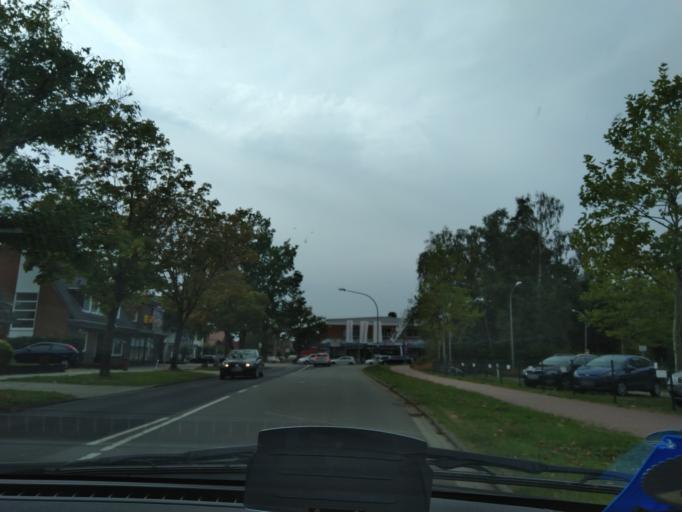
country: DE
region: Lower Saxony
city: Meppen
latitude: 52.6831
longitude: 7.2927
